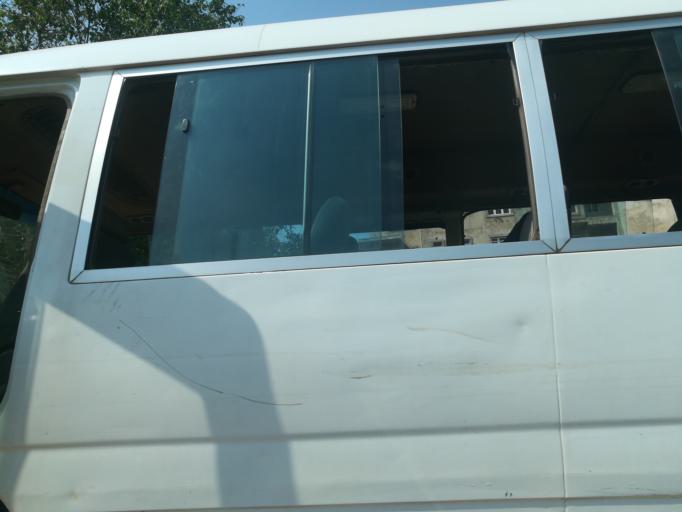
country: NG
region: Abuja Federal Capital Territory
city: Abuja
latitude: 9.0605
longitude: 7.4275
